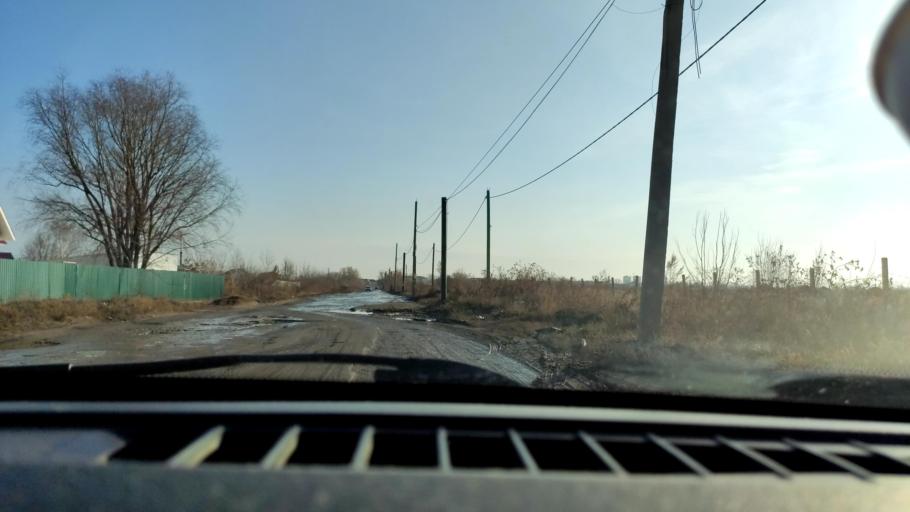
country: RU
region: Samara
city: Samara
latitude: 53.1190
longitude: 50.1035
